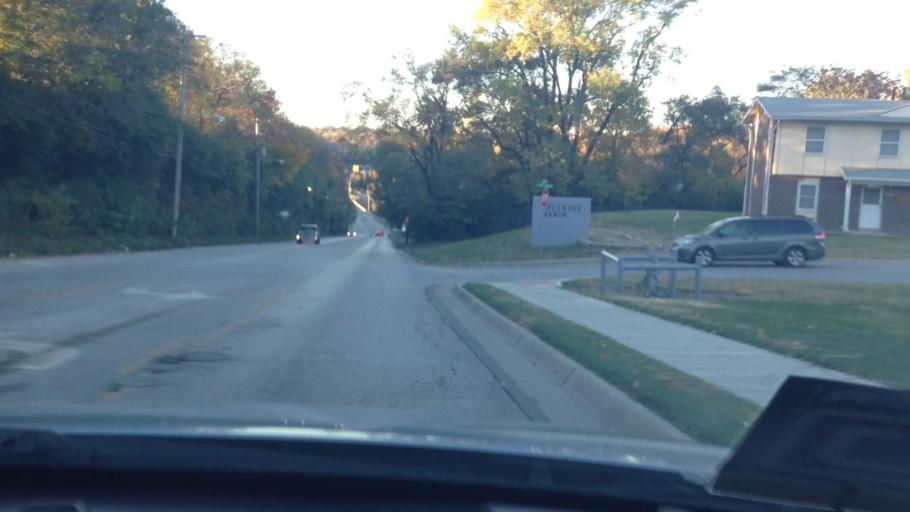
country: US
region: Kansas
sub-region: Johnson County
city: Westwood
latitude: 39.0532
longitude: -94.6215
